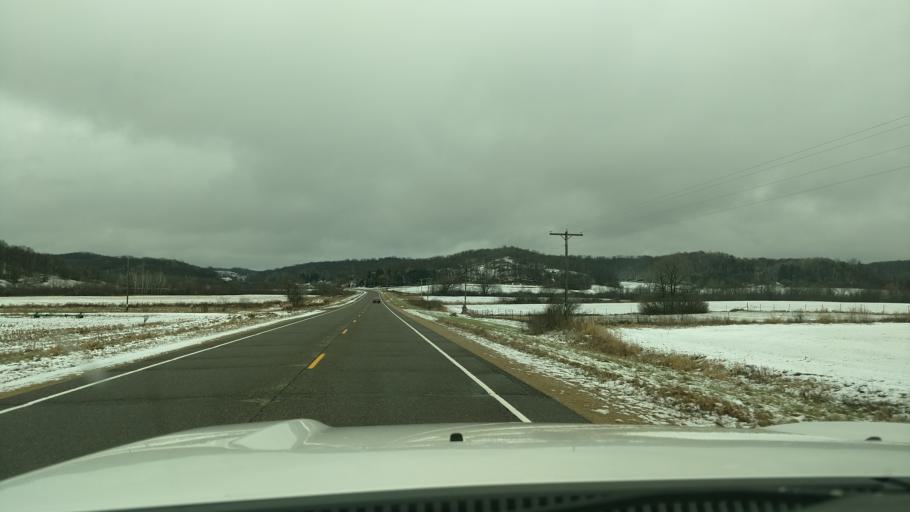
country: US
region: Wisconsin
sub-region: Dunn County
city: Tainter Lake
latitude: 45.1255
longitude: -91.8565
